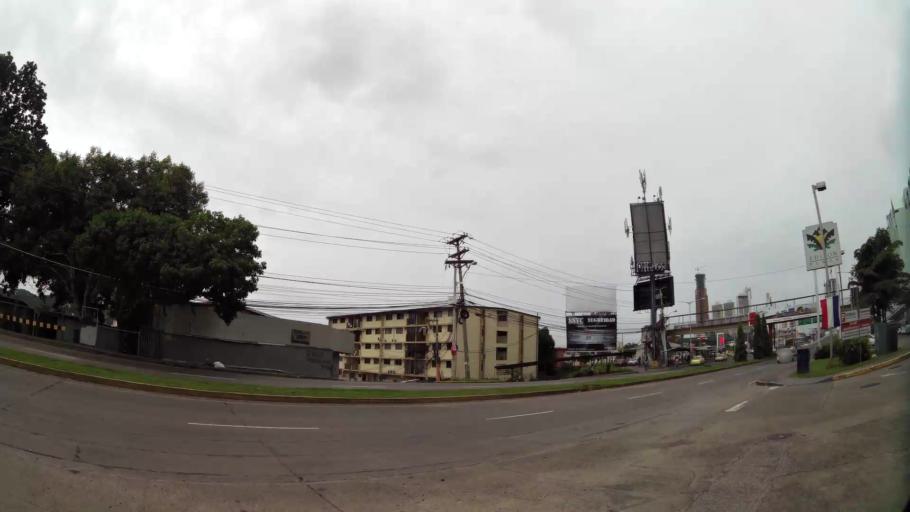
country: PA
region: Panama
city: Panama
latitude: 8.9928
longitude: -79.5341
